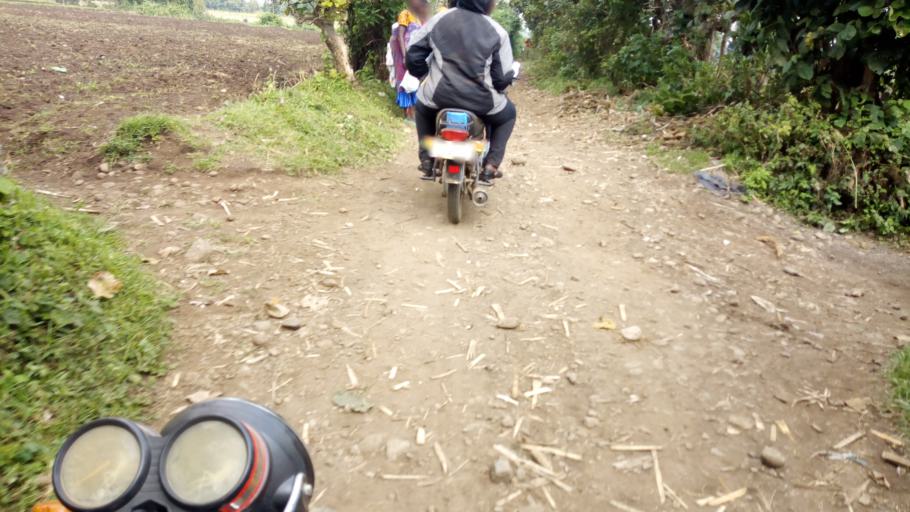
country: UG
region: Western Region
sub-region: Kisoro District
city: Kisoro
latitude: -1.3333
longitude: 29.6063
